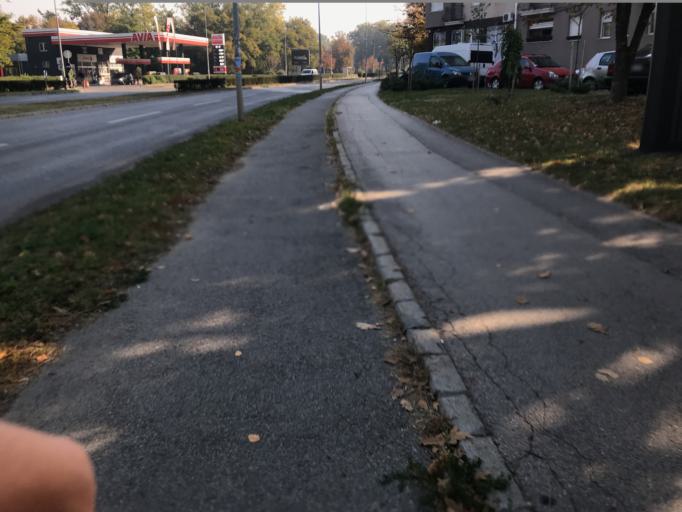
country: RS
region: Autonomna Pokrajina Vojvodina
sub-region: Juznobacki Okrug
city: Novi Sad
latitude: 45.2638
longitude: 19.8209
